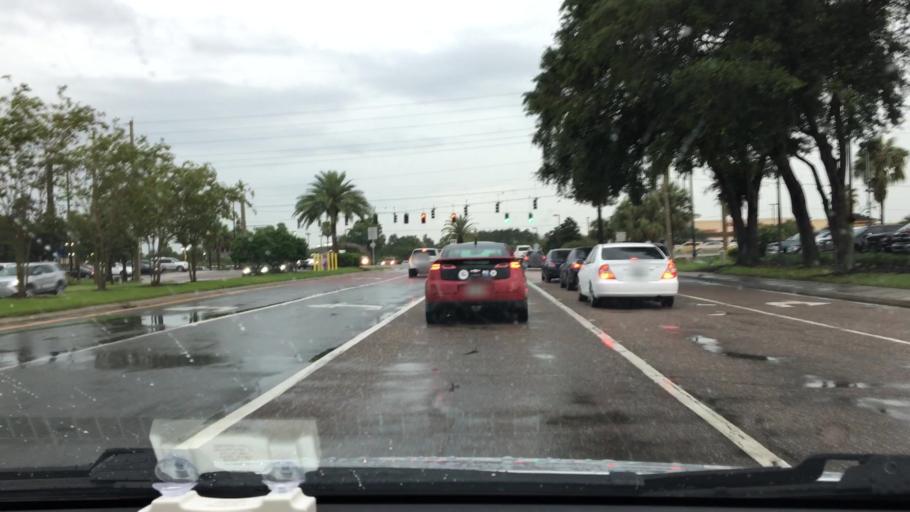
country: US
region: Florida
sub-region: Orange County
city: Conway
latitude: 28.4688
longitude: -81.3112
